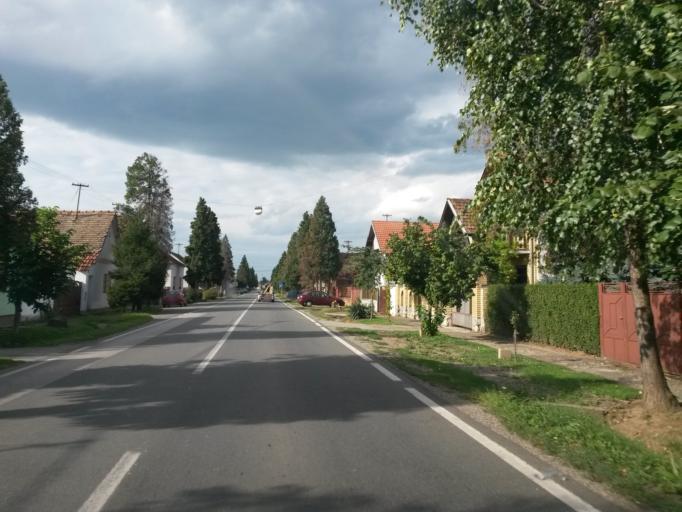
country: HR
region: Vukovarsko-Srijemska
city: Jarmina
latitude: 45.3118
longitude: 18.7348
